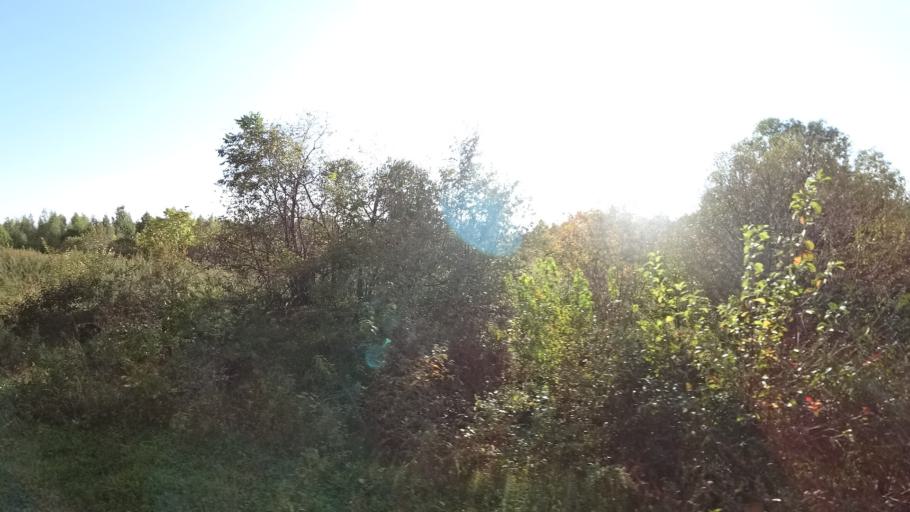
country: RU
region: Amur
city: Arkhara
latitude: 49.3494
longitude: 130.1154
